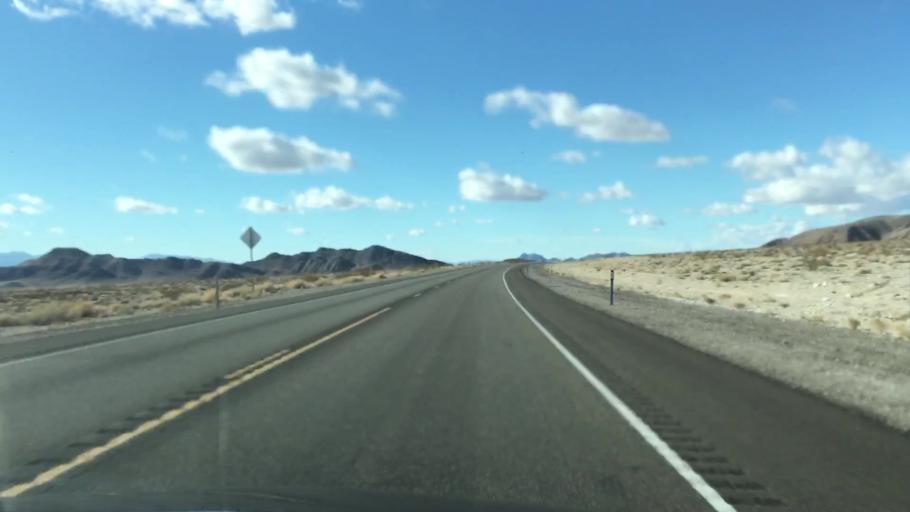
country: US
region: Nevada
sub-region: Nye County
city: Pahrump
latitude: 36.5730
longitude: -116.1819
